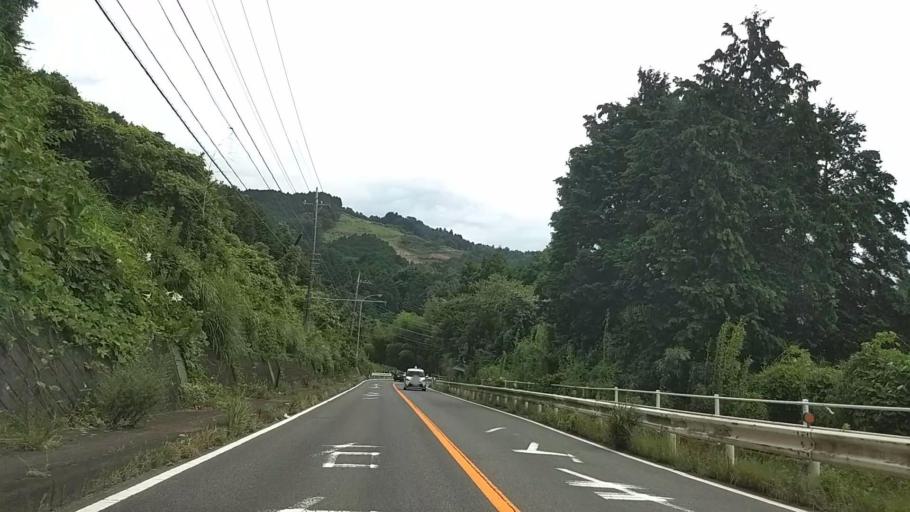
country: JP
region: Kanagawa
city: Hakone
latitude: 35.1469
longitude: 138.9803
